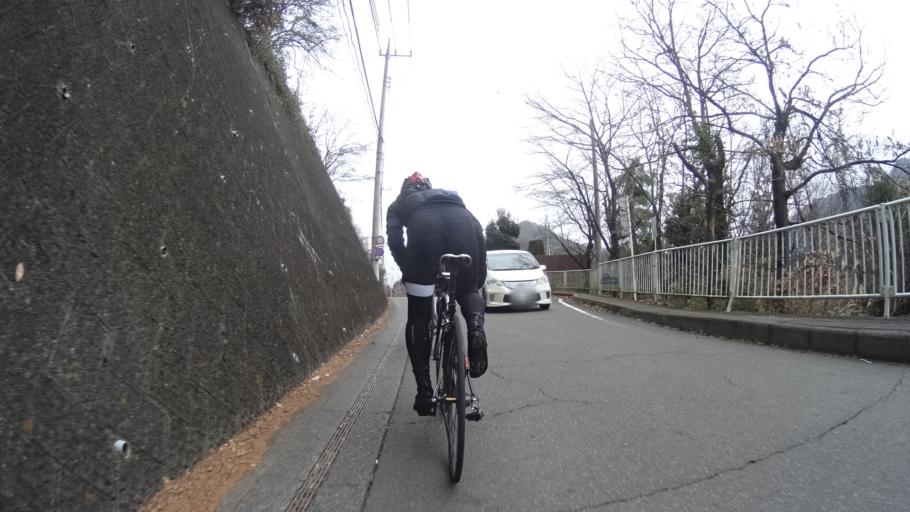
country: JP
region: Yamanashi
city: Otsuki
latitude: 35.6045
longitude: 138.9363
